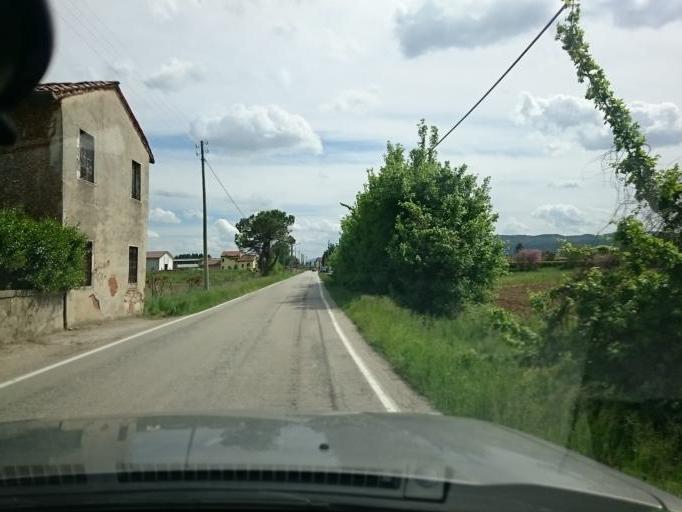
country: IT
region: Veneto
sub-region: Provincia di Vicenza
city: Vicenza
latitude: 45.5228
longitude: 11.5793
